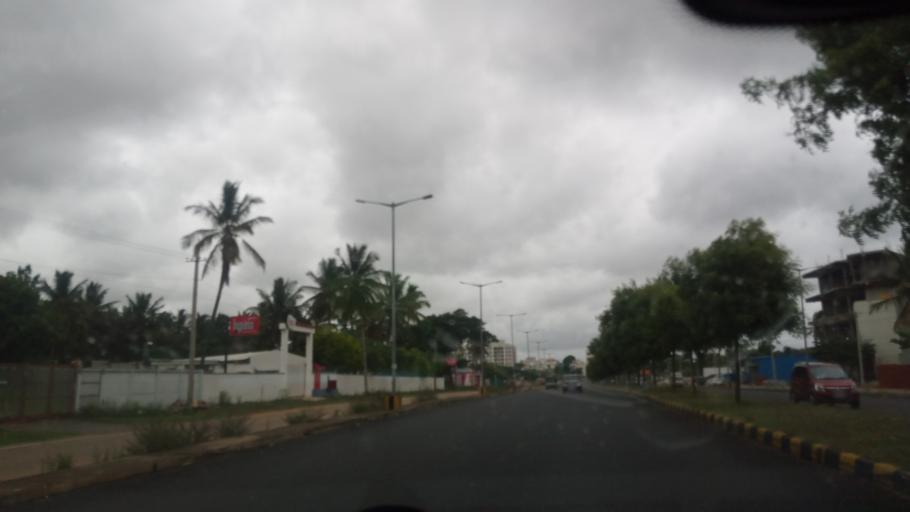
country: IN
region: Karnataka
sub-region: Mysore
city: Mysore
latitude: 12.3108
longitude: 76.5972
